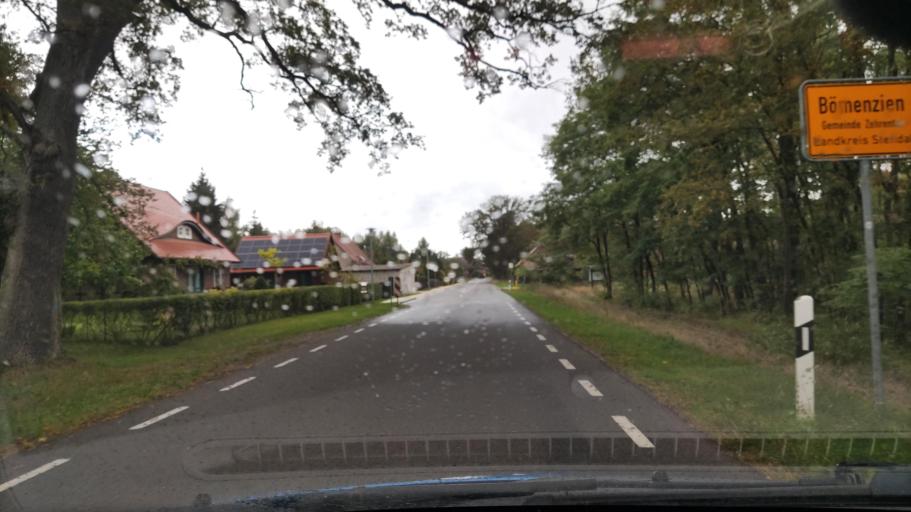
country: DE
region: Lower Saxony
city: Gartow
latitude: 52.9858
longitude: 11.5459
